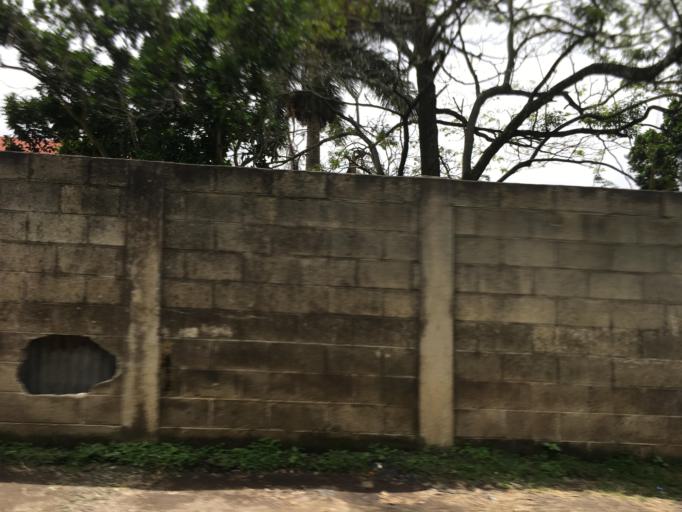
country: GT
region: Guatemala
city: Villa Canales
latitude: 14.4462
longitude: -90.5636
